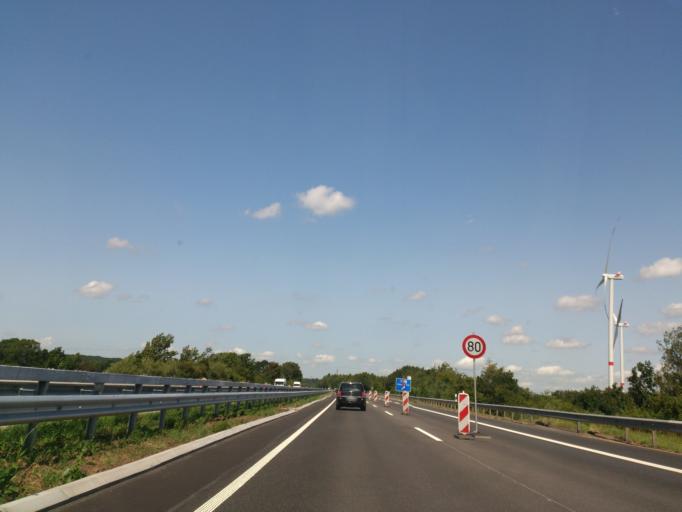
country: DE
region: Schleswig-Holstein
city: Arkebek
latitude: 54.1328
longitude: 9.2531
